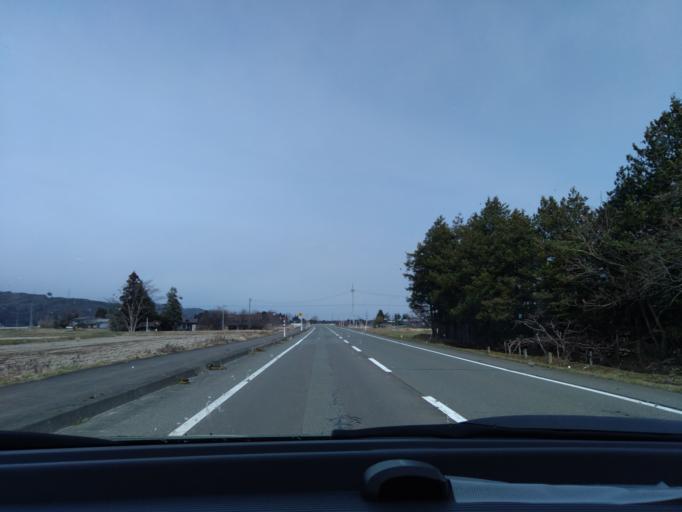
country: JP
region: Iwate
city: Morioka-shi
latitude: 39.5736
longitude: 141.1096
